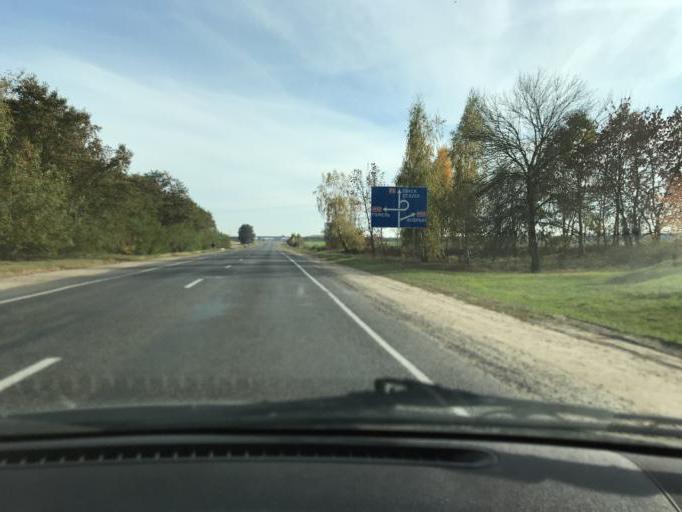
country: BY
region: Brest
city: Asnyezhytsy
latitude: 52.1916
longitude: 26.0735
